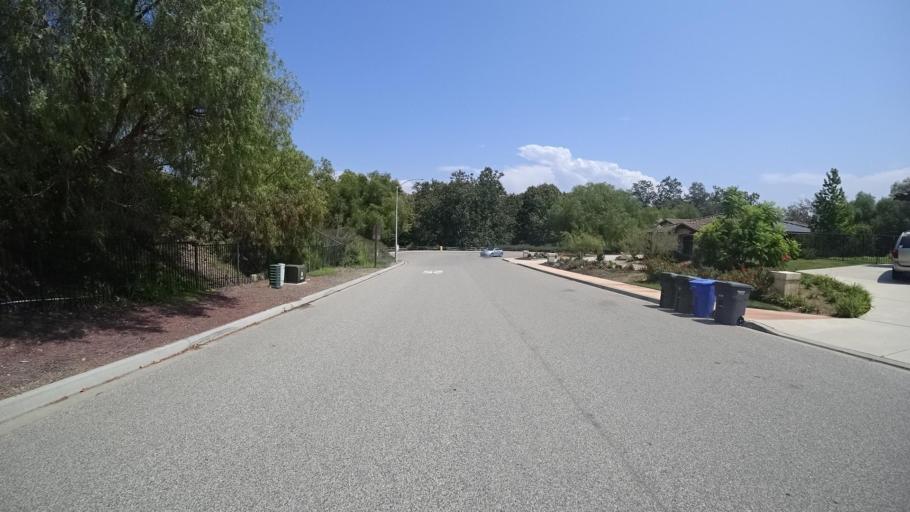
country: US
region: California
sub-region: San Diego County
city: Bonsall
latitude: 33.3163
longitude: -117.1993
